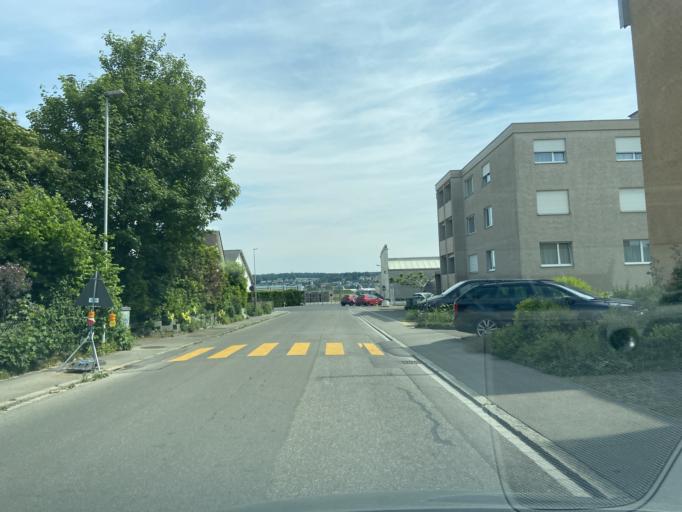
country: CH
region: Zurich
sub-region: Bezirk Uster
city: Duebendorf / Kunklerstrasse
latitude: 47.3987
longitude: 8.6299
